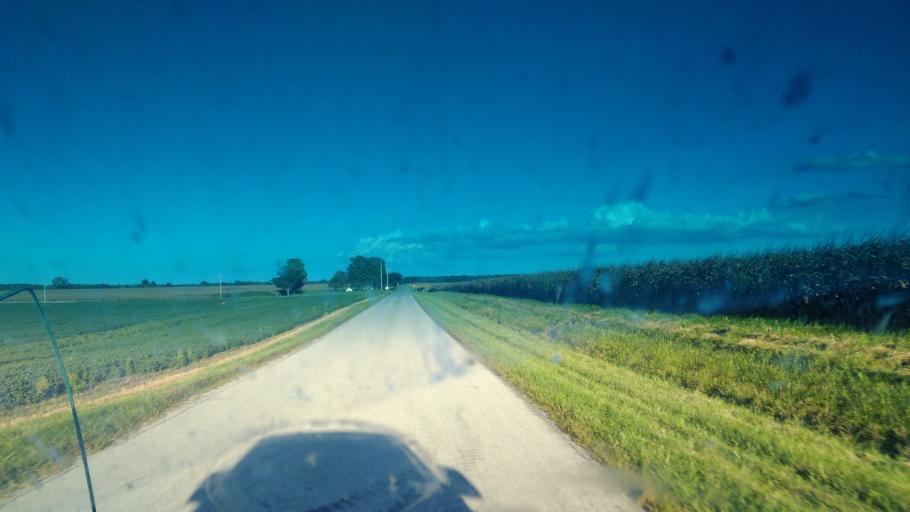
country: US
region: Ohio
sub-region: Wyandot County
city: Upper Sandusky
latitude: 40.8909
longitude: -83.2795
